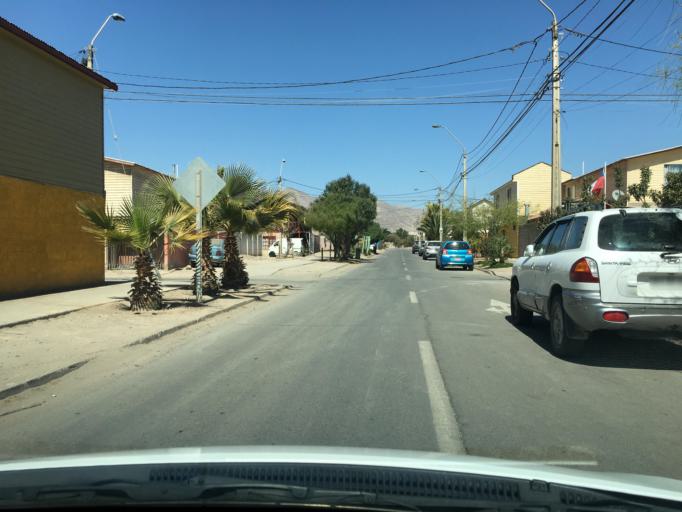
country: CL
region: Atacama
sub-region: Provincia de Copiapo
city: Copiapo
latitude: -27.4076
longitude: -70.2858
